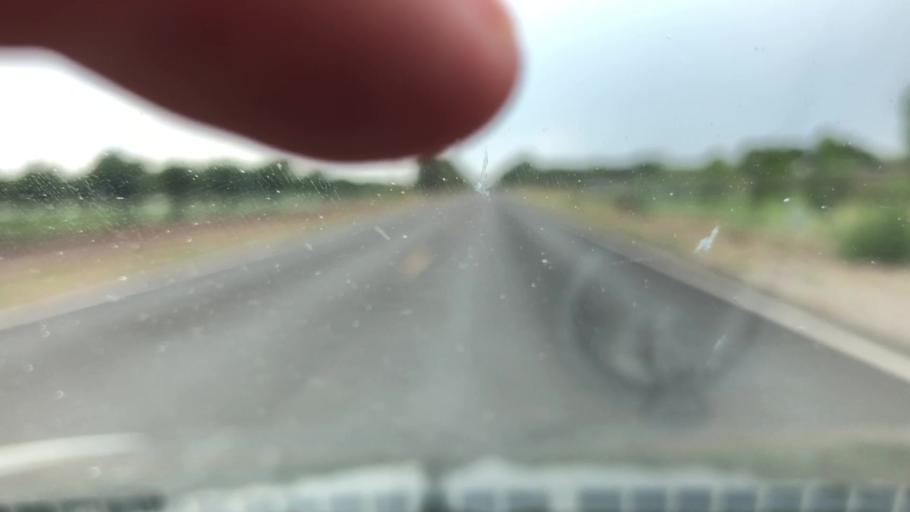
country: US
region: Texas
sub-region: El Paso County
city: Canutillo
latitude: 31.9225
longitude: -106.6272
